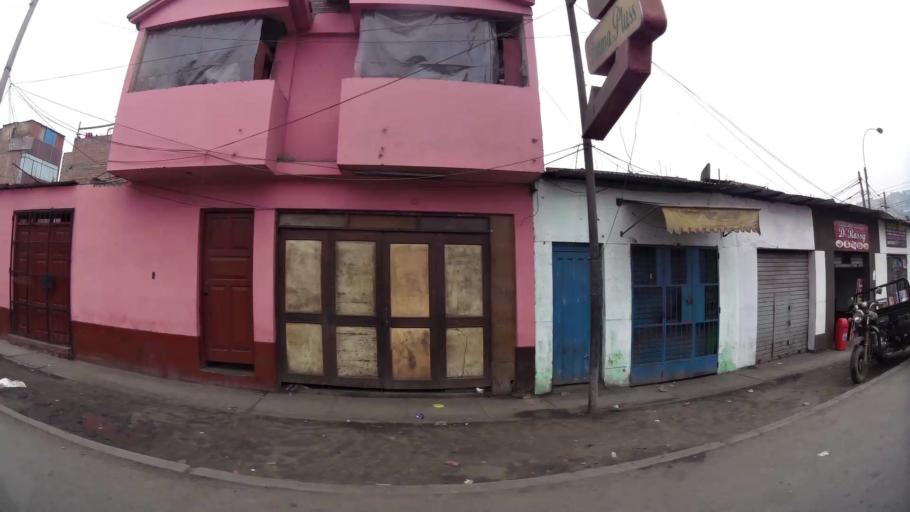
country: PE
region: Lima
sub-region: Lima
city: Urb. Santo Domingo
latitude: -11.9335
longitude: -76.9685
